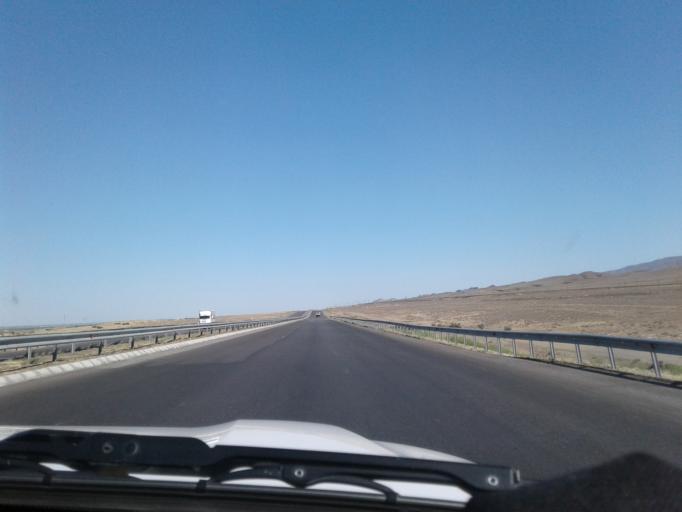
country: IR
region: Razavi Khorasan
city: Dargaz
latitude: 37.6794
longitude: 59.0871
